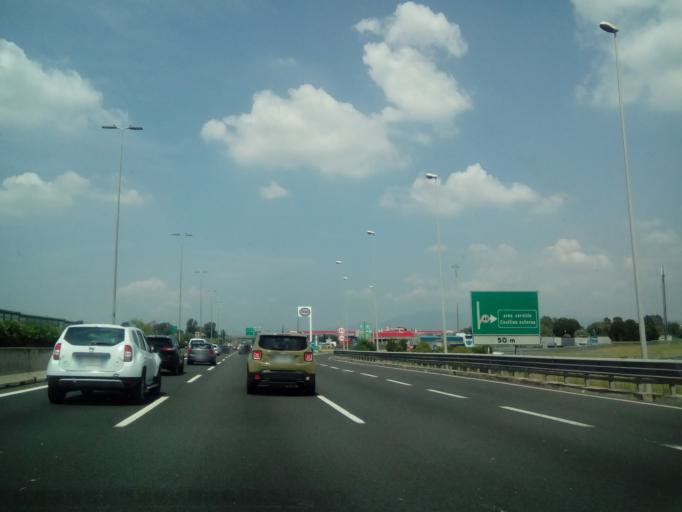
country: IT
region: Latium
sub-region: Citta metropolitana di Roma Capitale
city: Ciampino
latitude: 41.8727
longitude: 12.6057
